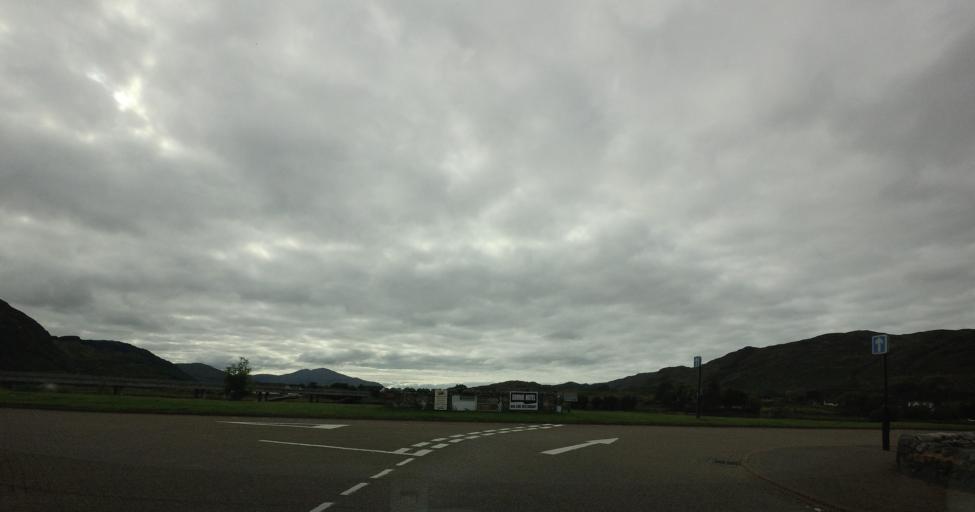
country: GB
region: Scotland
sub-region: Highland
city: Fort William
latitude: 57.2790
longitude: -5.5157
